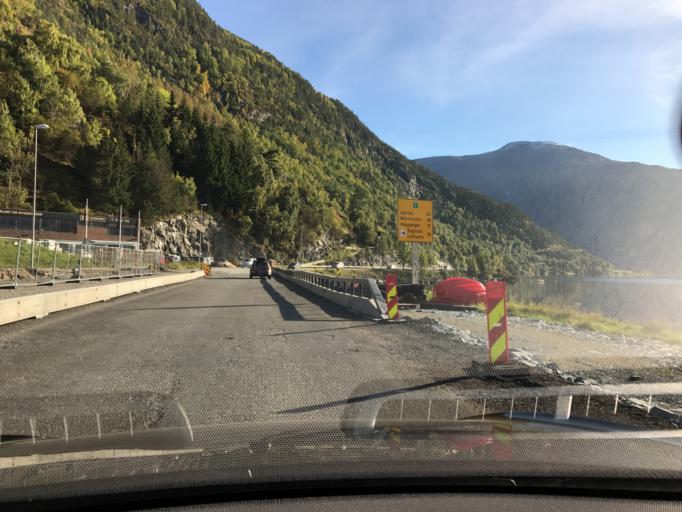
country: NO
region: Sogn og Fjordane
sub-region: Sogndal
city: Sogndalsfjora
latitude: 61.2294
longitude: 7.1244
